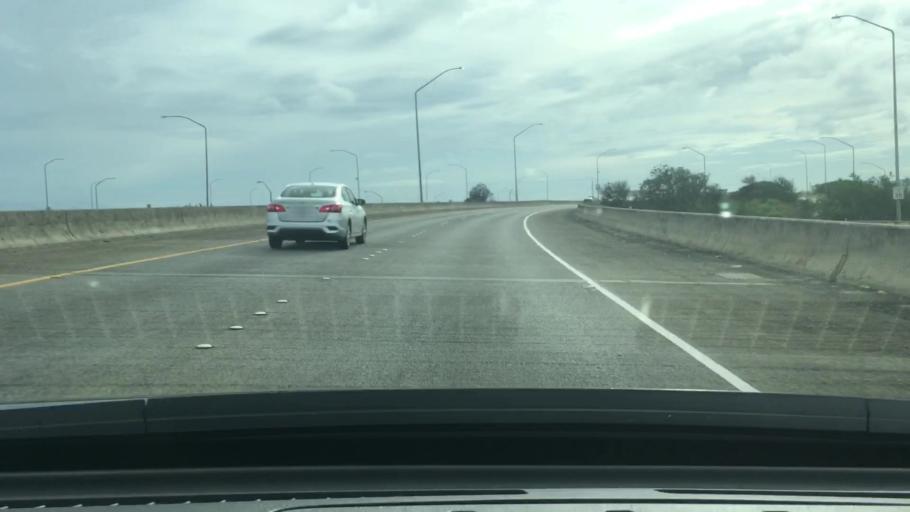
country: US
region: Hawaii
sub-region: Honolulu County
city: Honolulu
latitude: 21.3347
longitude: -157.8898
